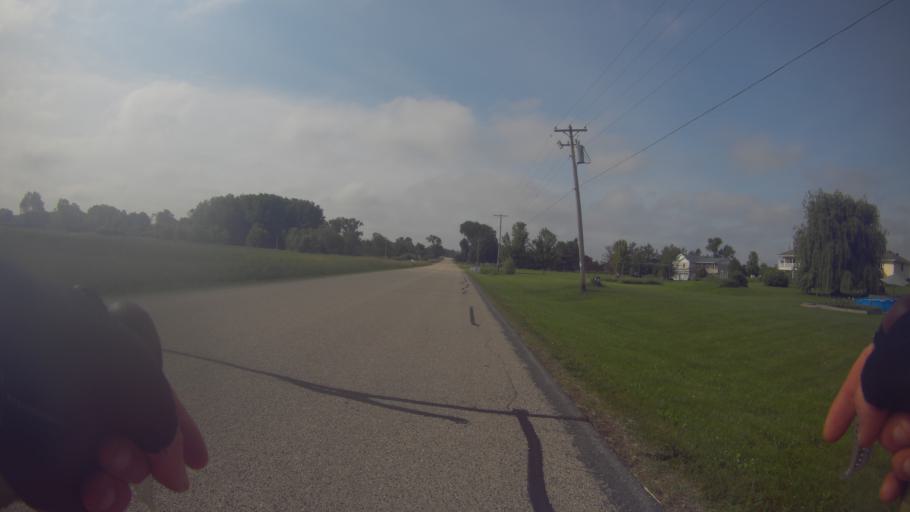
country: US
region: Wisconsin
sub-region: Dane County
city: McFarland
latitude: 42.9998
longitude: -89.2352
